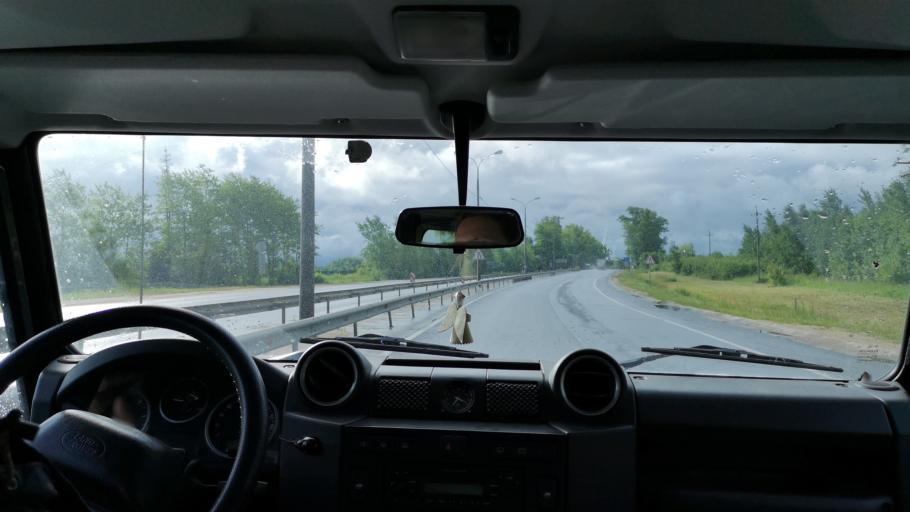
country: RU
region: Moskovskaya
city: Dmitrov
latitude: 56.3642
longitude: 37.4780
